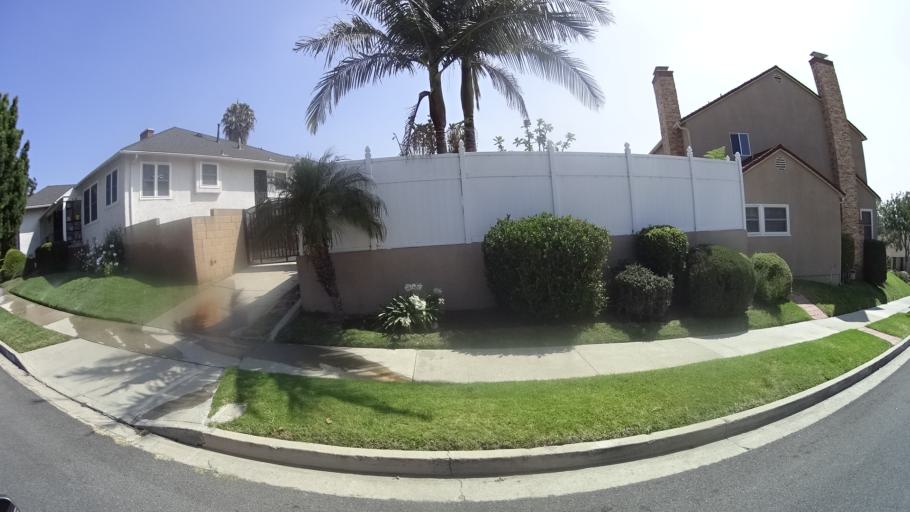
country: US
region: California
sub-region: Los Angeles County
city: View Park-Windsor Hills
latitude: 33.9972
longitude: -118.3445
